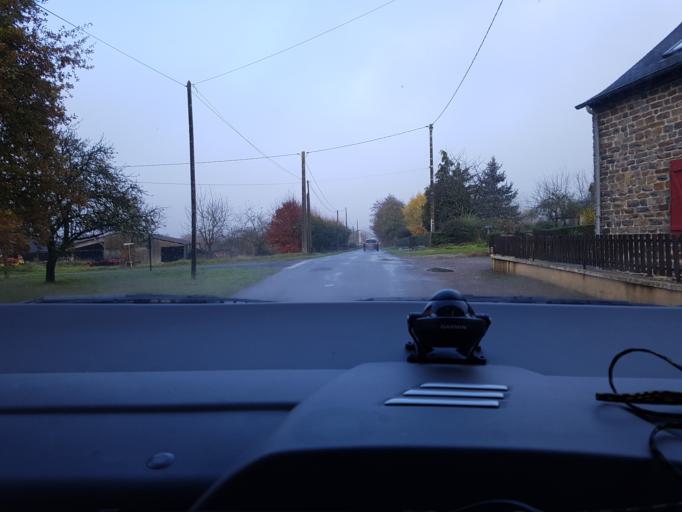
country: FR
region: Brittany
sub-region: Departement d'Ille-et-Vilaine
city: Livre-sur-Changeon
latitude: 48.1889
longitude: -1.3605
